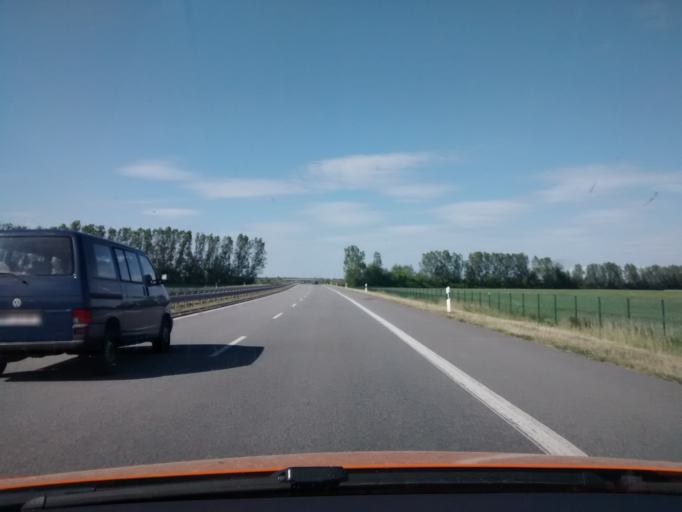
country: DE
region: Brandenburg
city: Trebbin
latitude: 52.1683
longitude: 13.2420
